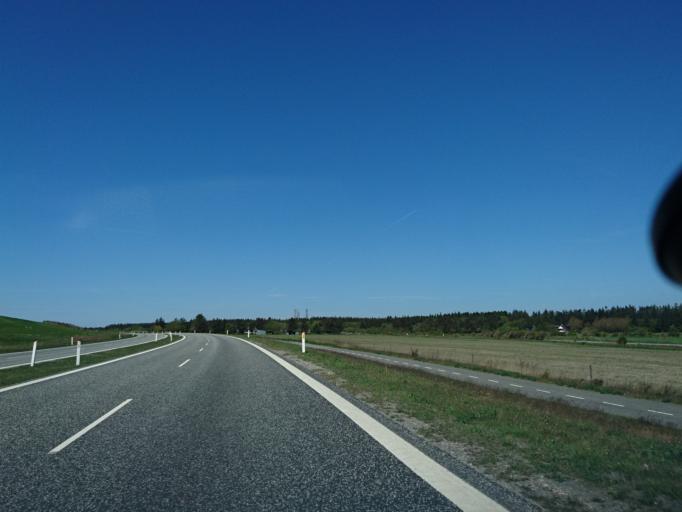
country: DK
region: North Denmark
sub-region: Hjorring Kommune
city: Hirtshals
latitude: 57.5688
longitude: 10.0112
